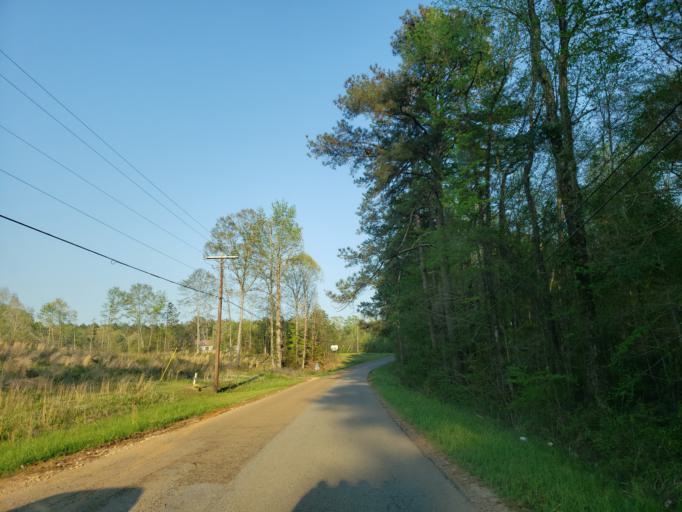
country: US
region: Mississippi
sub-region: Lauderdale County
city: Marion
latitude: 32.3989
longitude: -88.5870
